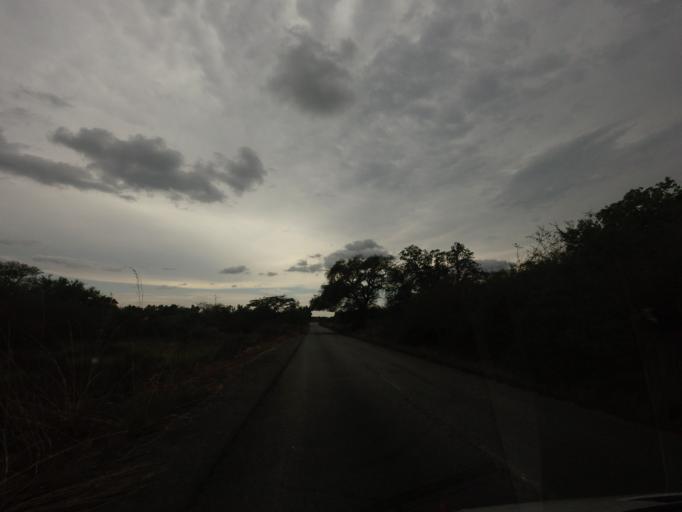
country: ZA
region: Limpopo
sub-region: Mopani District Municipality
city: Hoedspruit
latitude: -24.5296
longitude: 30.9897
